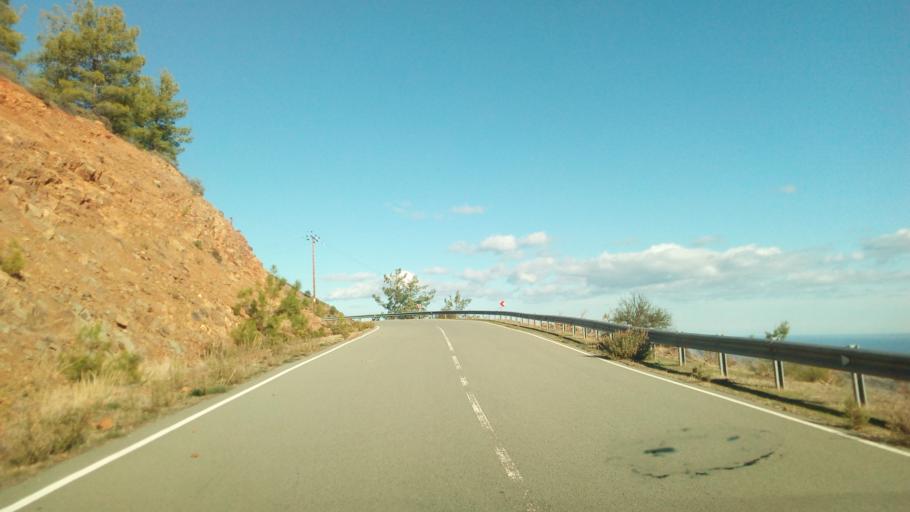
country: CY
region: Lefkosia
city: Kato Pyrgos
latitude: 35.1165
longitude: 32.7348
